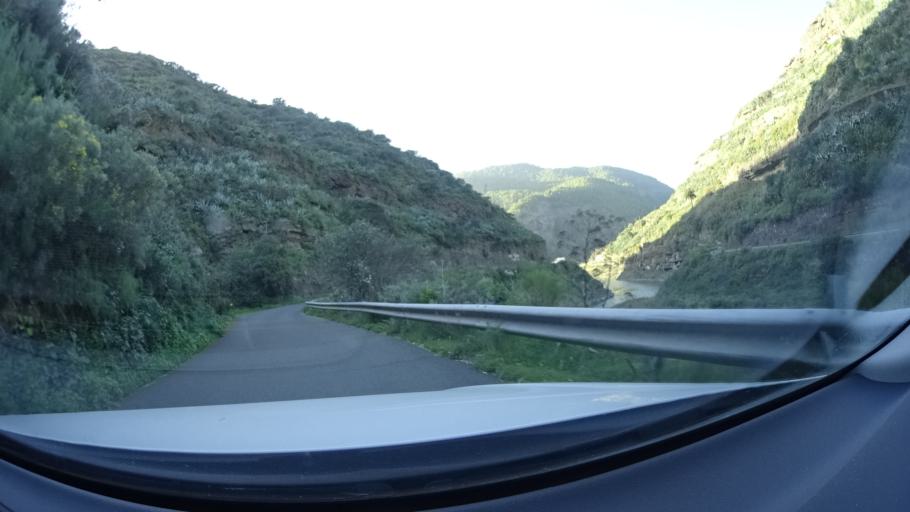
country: ES
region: Canary Islands
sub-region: Provincia de Las Palmas
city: Artenara
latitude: 28.0453
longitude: -15.6644
